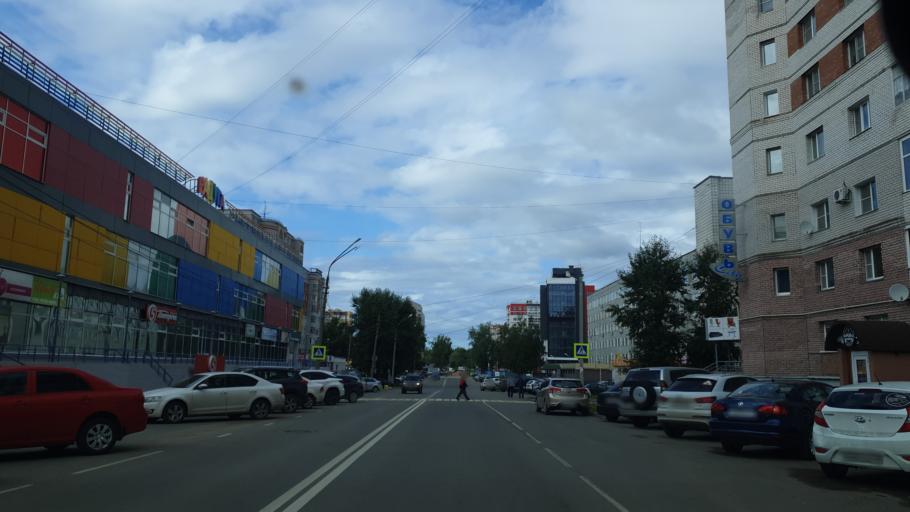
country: RU
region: Komi Republic
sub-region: Syktyvdinskiy Rayon
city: Syktyvkar
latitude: 61.6729
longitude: 50.8250
